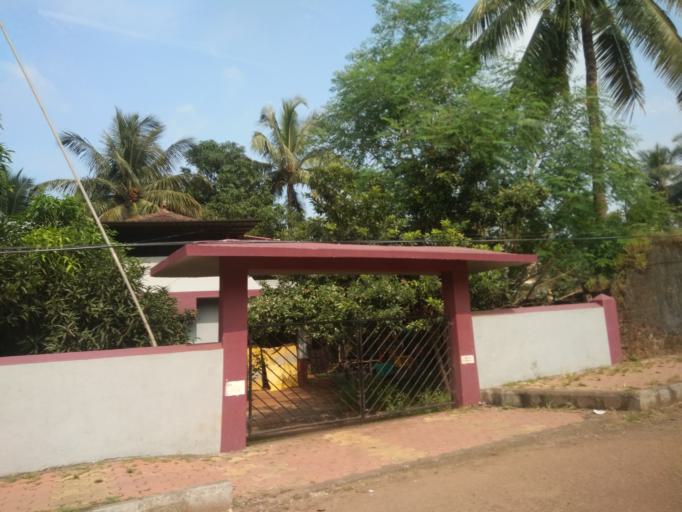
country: IN
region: Goa
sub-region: North Goa
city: Serula
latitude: 15.5335
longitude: 73.8224
